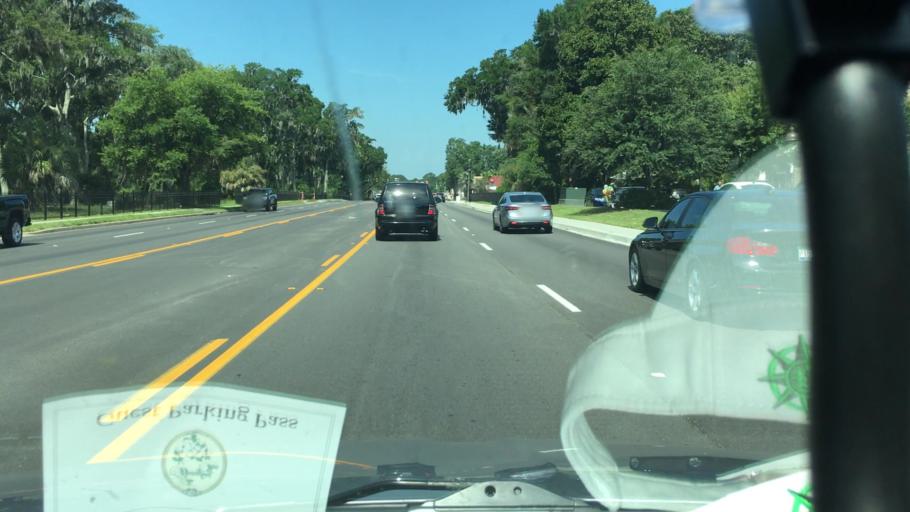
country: US
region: South Carolina
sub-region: Beaufort County
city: Beaufort
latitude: 32.4409
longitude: -80.6888
